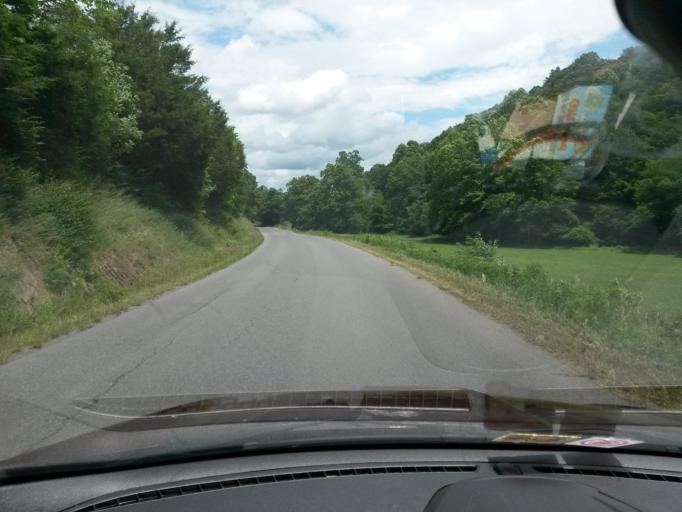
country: US
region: West Virginia
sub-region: Monroe County
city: Union
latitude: 37.5049
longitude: -80.5817
